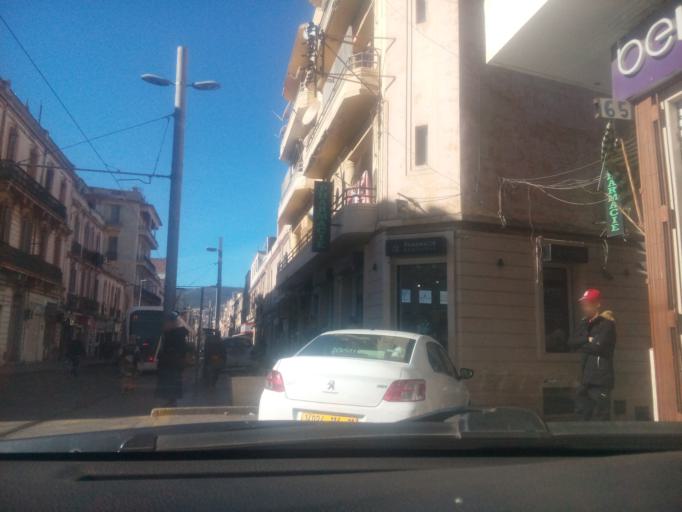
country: DZ
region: Oran
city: Oran
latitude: 35.6998
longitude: -0.6378
